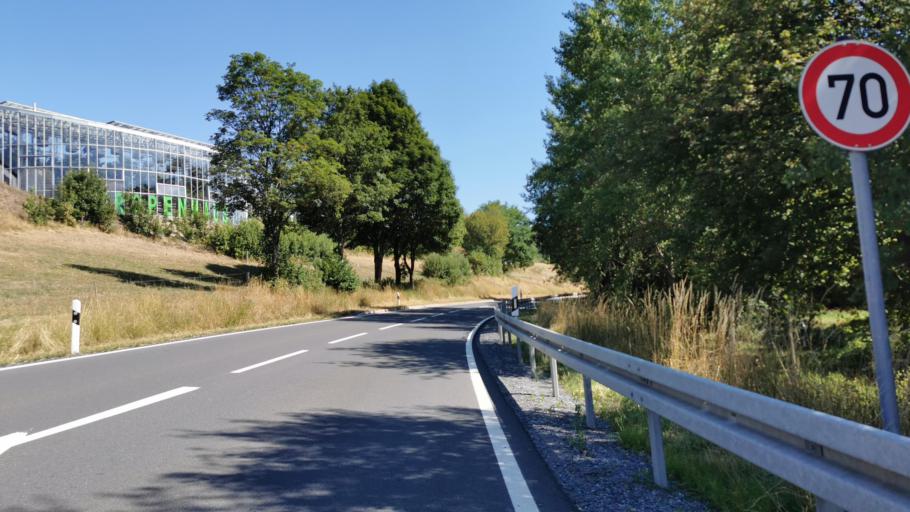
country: DE
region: Bavaria
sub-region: Upper Franconia
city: Tettau
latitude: 50.4677
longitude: 11.2761
